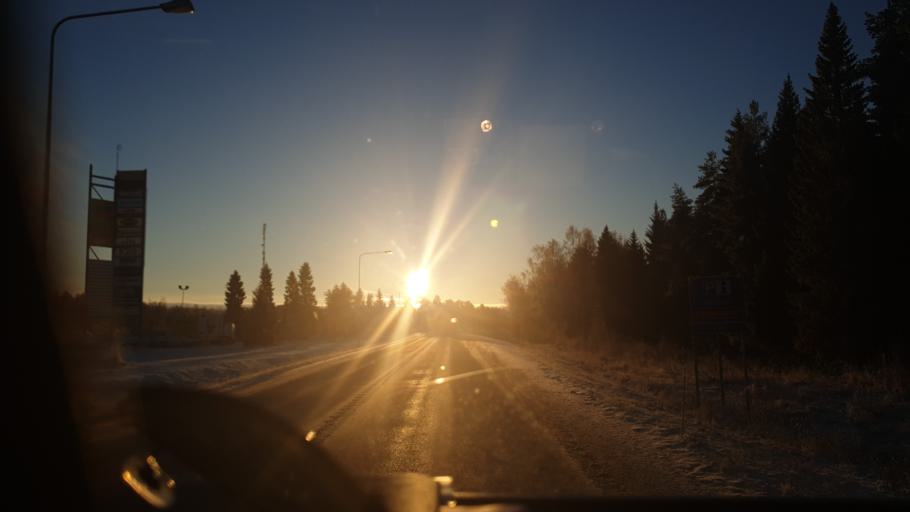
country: FI
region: Northern Ostrobothnia
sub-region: Ylivieska
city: Kalajoki
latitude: 64.2853
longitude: 23.9471
